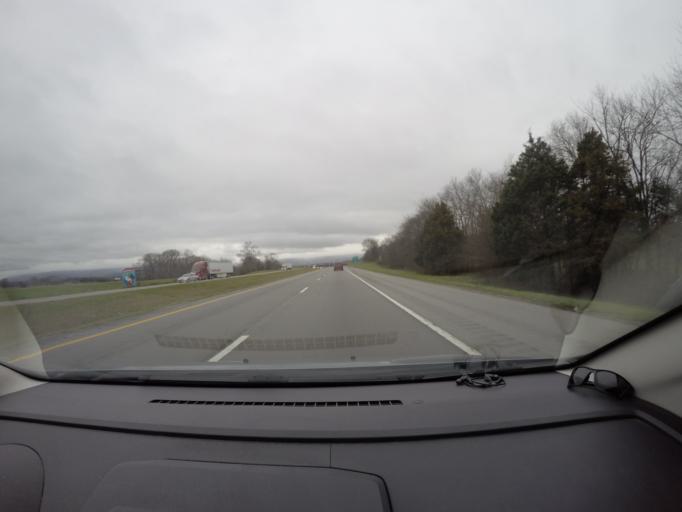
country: US
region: Tennessee
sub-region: Marion County
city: Monteagle
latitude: 35.3040
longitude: -85.9068
